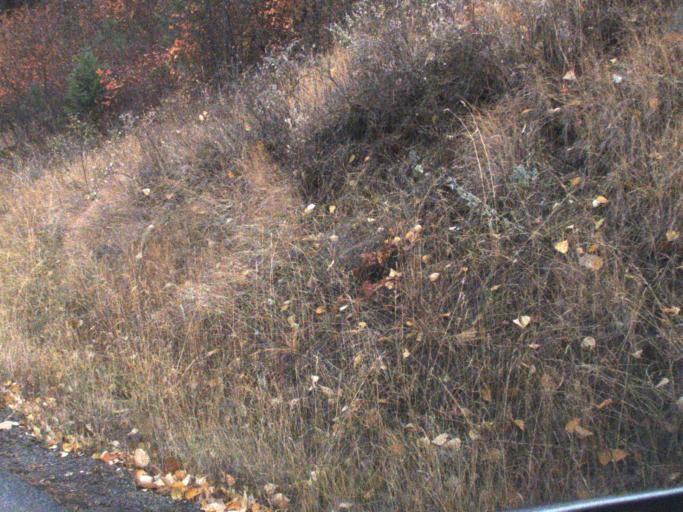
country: US
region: Washington
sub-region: Lincoln County
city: Davenport
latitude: 48.1177
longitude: -118.1974
